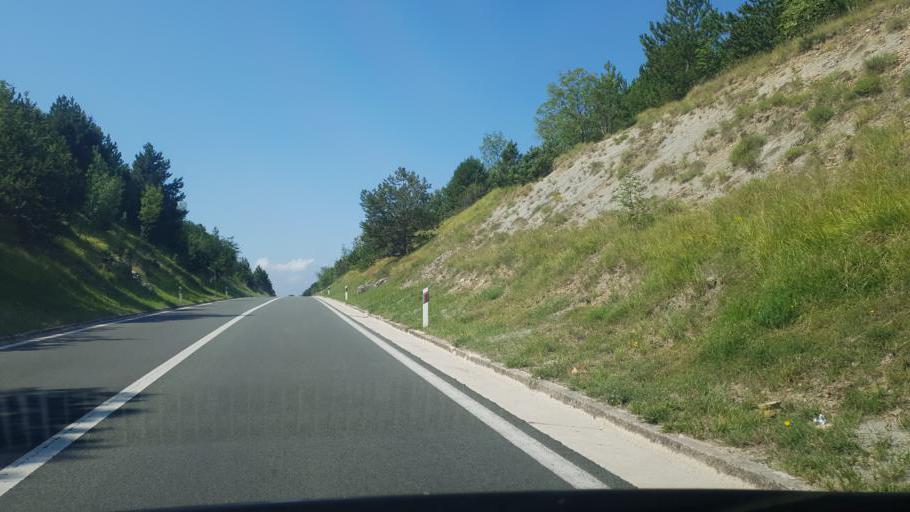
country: HR
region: Istarska
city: Buzet
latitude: 45.3362
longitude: 14.0780
